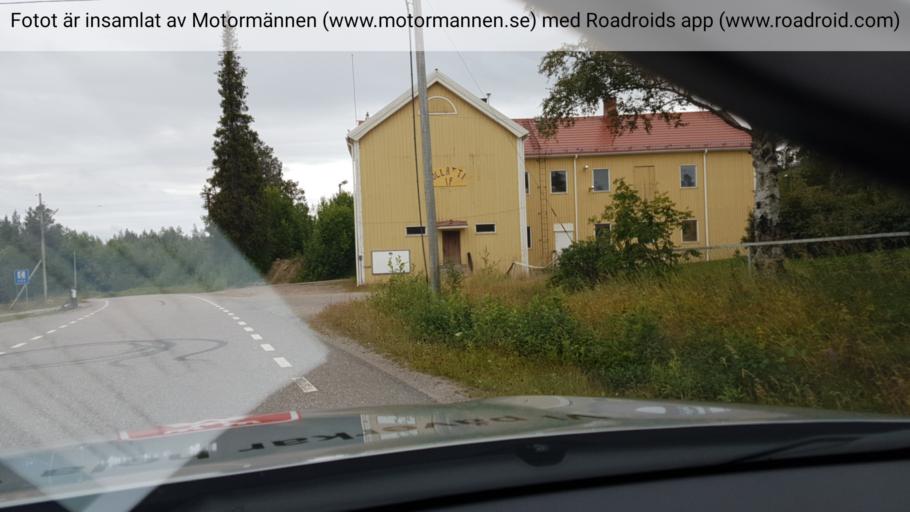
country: SE
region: Norrbotten
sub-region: Gallivare Kommun
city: Gaellivare
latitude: 67.0139
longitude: 21.8155
